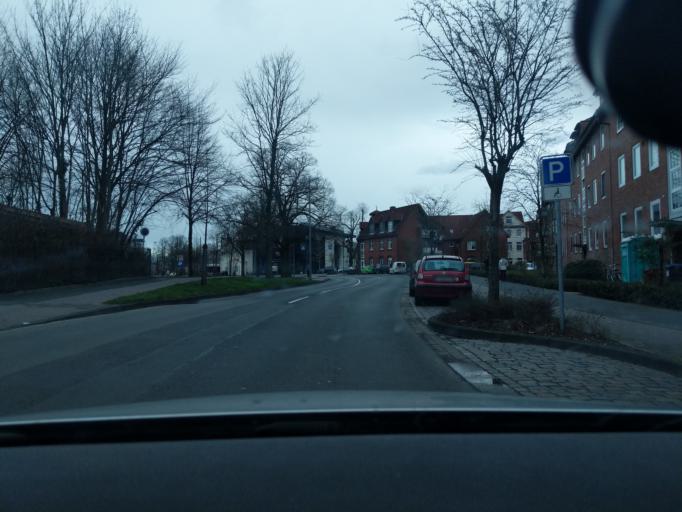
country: DE
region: Lower Saxony
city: Stade
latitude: 53.6039
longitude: 9.4733
